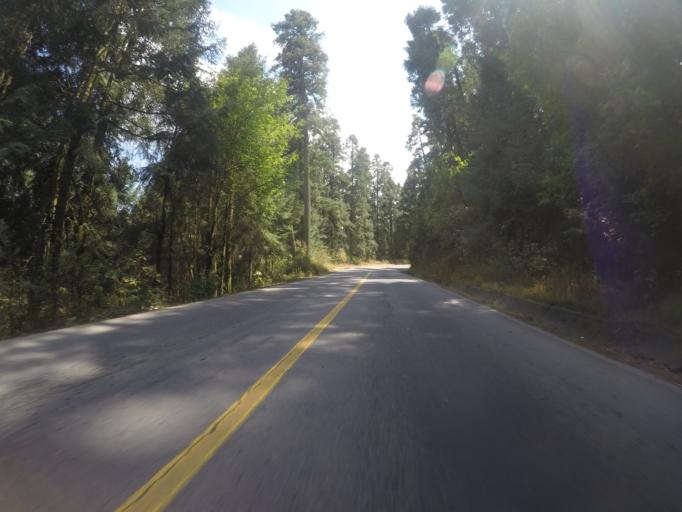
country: MX
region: Mexico
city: Cerro La Calera
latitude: 19.1871
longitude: -99.8058
